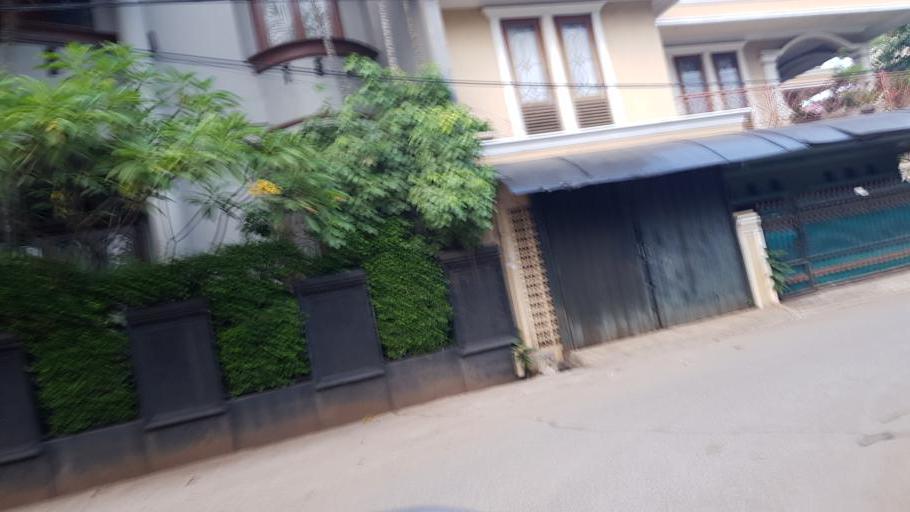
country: ID
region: West Java
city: Bekasi
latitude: -6.2673
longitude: 106.9474
